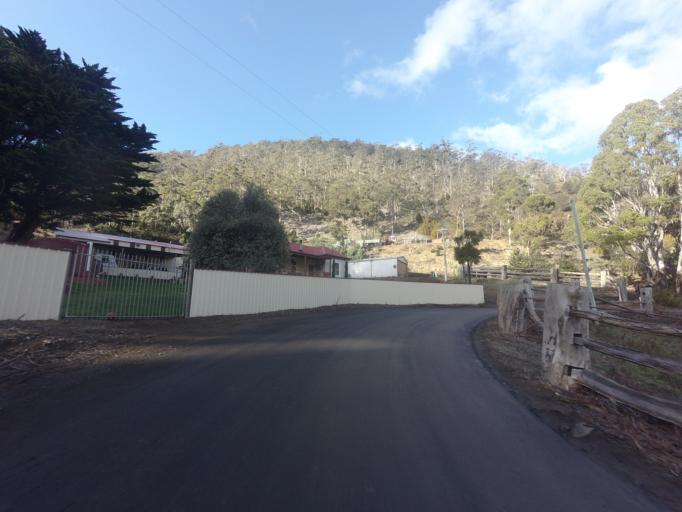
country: AU
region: Tasmania
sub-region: Glenorchy
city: Berriedale
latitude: -42.8174
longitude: 147.1791
